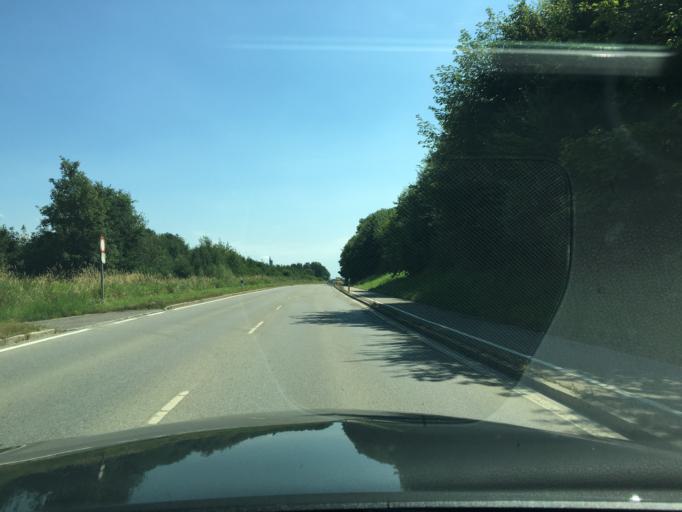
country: DE
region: Baden-Wuerttemberg
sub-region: Tuebingen Region
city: Dornstadt
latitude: 48.4274
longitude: 9.9475
